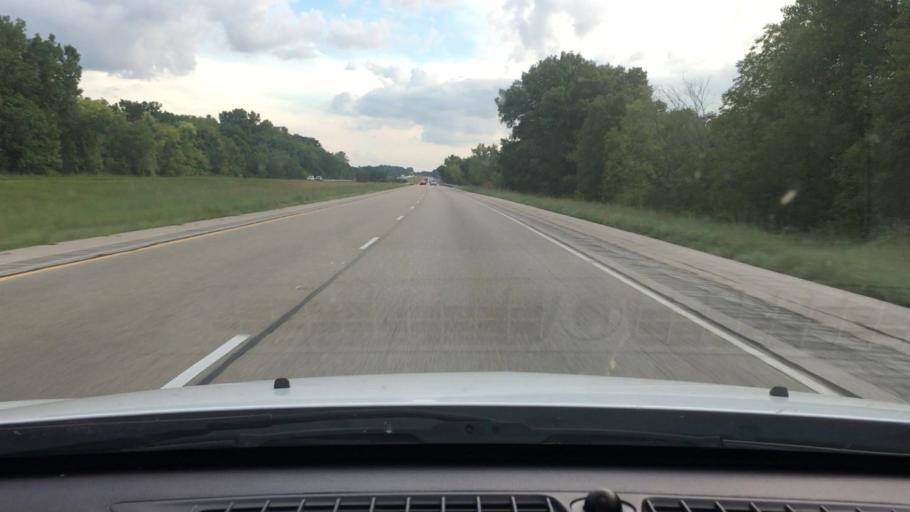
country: US
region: Illinois
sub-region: McLean County
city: Twin Grove
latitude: 40.3765
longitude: -89.0956
